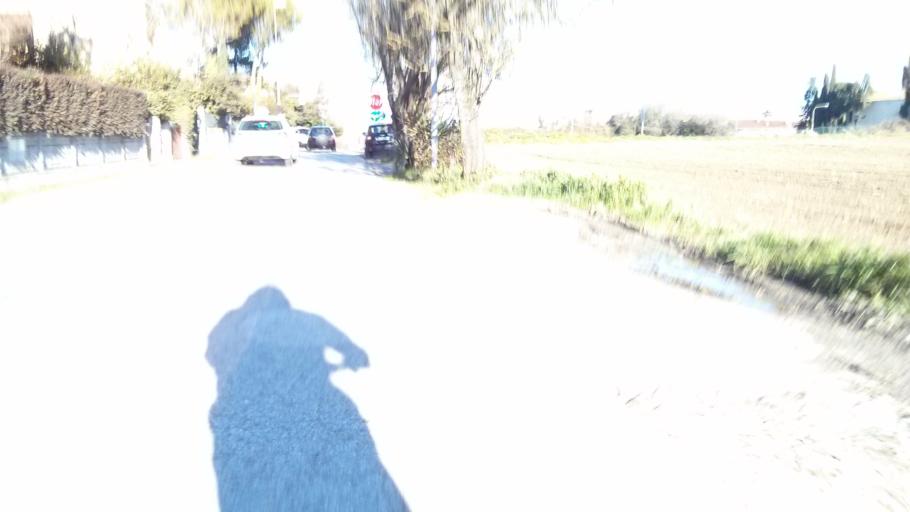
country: IT
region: The Marches
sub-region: Provincia di Pesaro e Urbino
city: Fano
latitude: 43.8453
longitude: 13.0072
